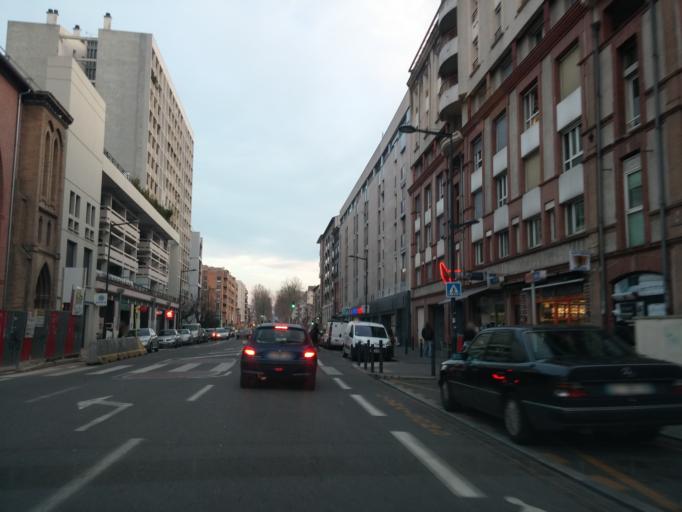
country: FR
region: Midi-Pyrenees
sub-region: Departement de la Haute-Garonne
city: Toulouse
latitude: 43.5856
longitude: 1.4474
